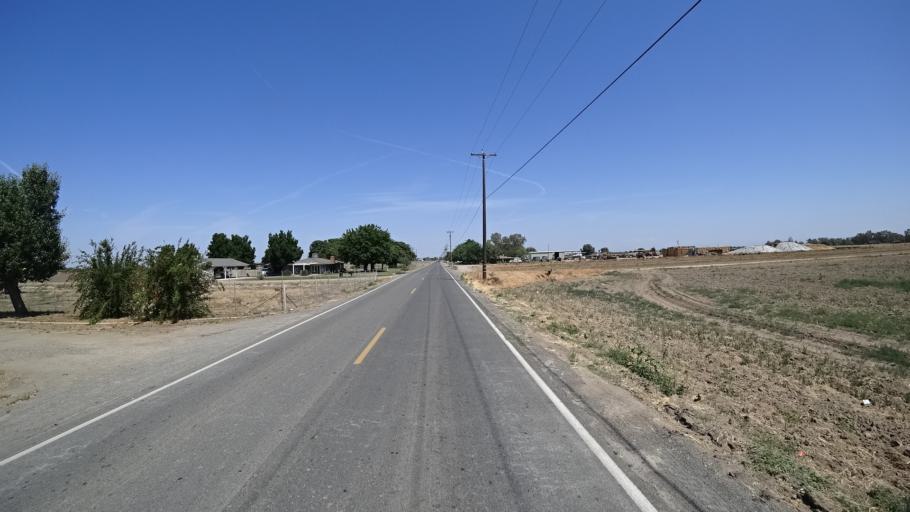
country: US
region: California
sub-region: Kings County
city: Lemoore
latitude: 36.2468
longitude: -119.7629
